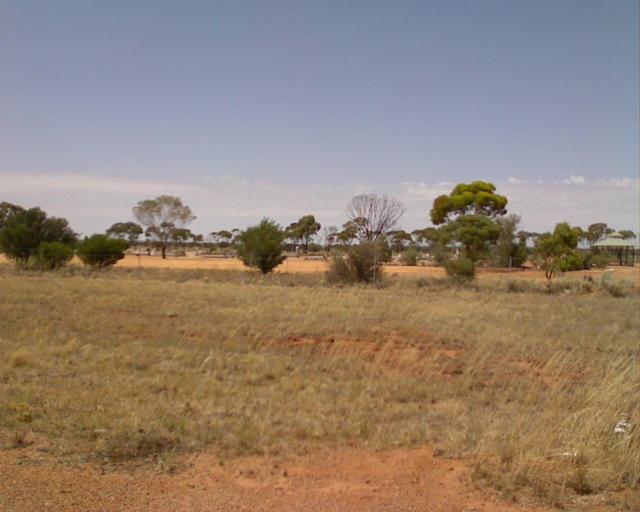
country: AU
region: Western Australia
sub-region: Merredin
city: Merredin
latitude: -30.9173
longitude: 118.2499
